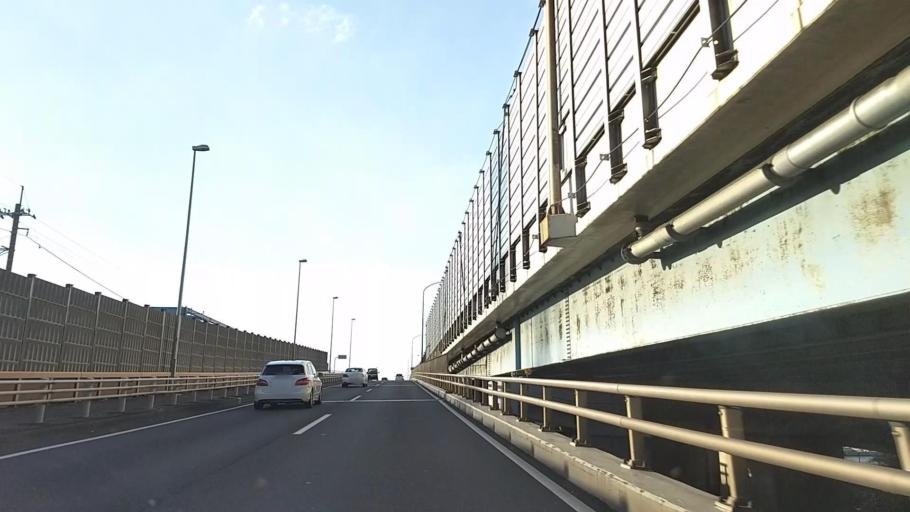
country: JP
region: Chiba
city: Funabashi
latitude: 35.6854
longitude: 139.9877
